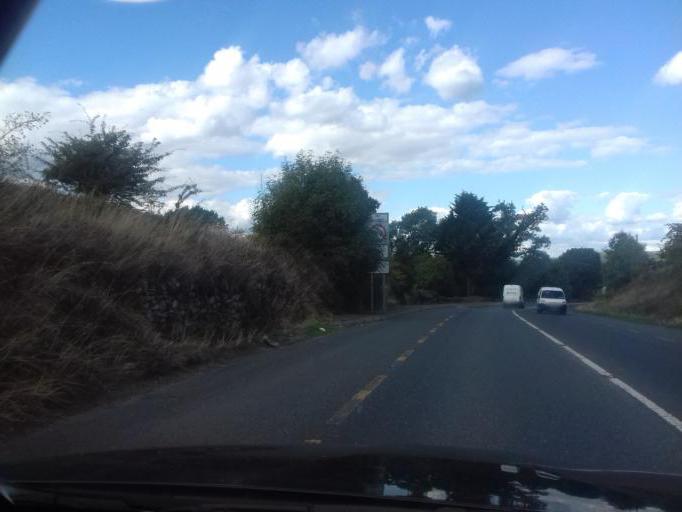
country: IE
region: Leinster
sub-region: Kilkenny
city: Thomastown
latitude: 52.5193
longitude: -7.1425
